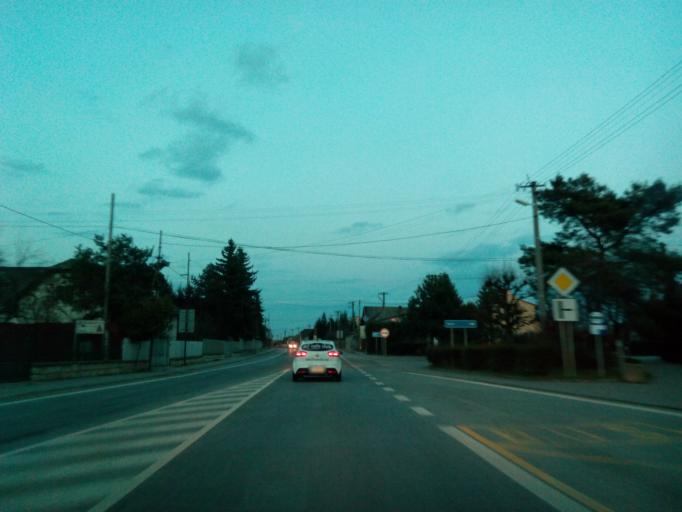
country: SK
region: Kosicky
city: Moldava nad Bodvou
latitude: 48.5981
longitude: 21.0649
